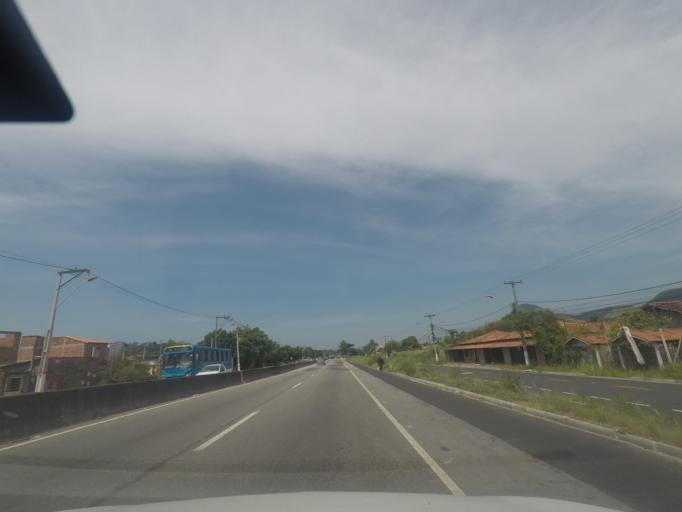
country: BR
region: Rio de Janeiro
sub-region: Marica
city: Marica
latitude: -22.9236
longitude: -42.8615
